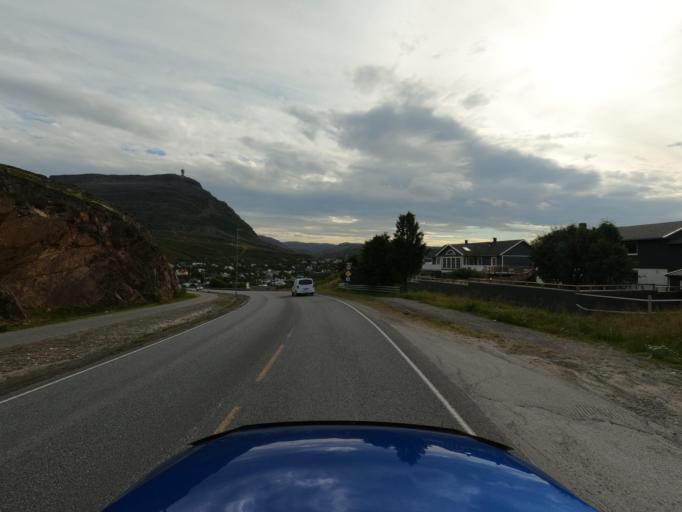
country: NO
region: Finnmark Fylke
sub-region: Hammerfest
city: Rypefjord
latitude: 70.6492
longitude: 23.6679
